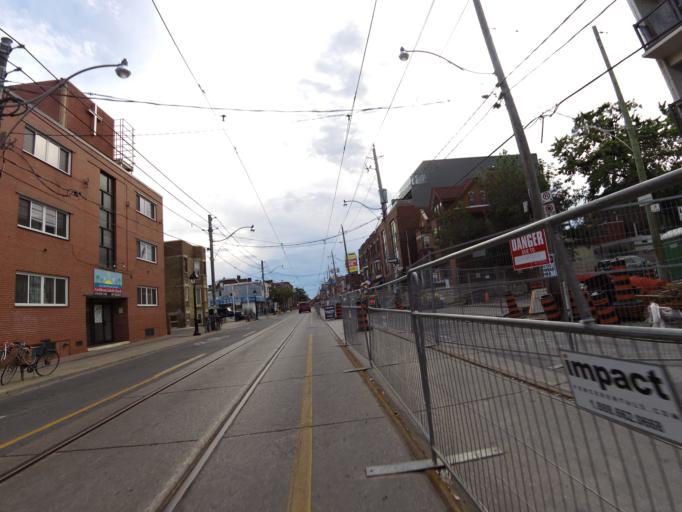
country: CA
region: Ontario
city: Toronto
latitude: 43.6541
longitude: -79.4241
